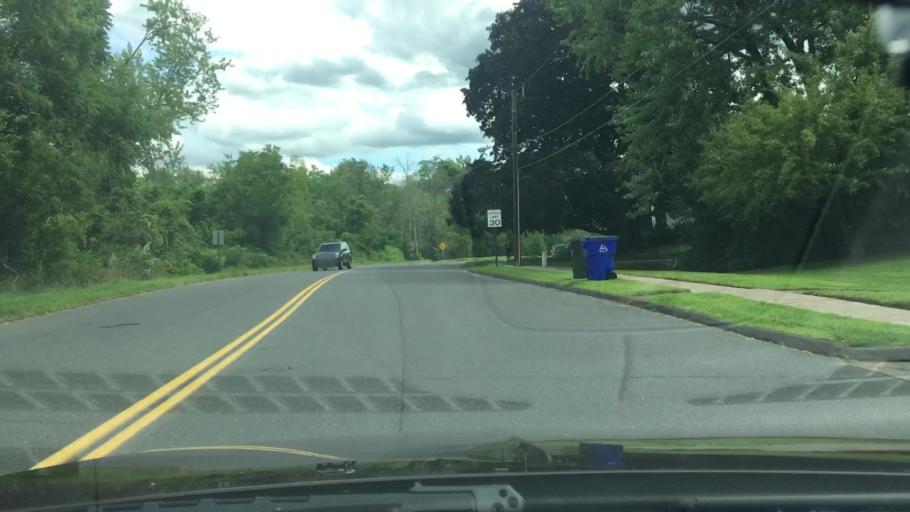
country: US
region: Connecticut
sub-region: Hartford County
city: Wethersfield
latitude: 41.7039
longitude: -72.6580
